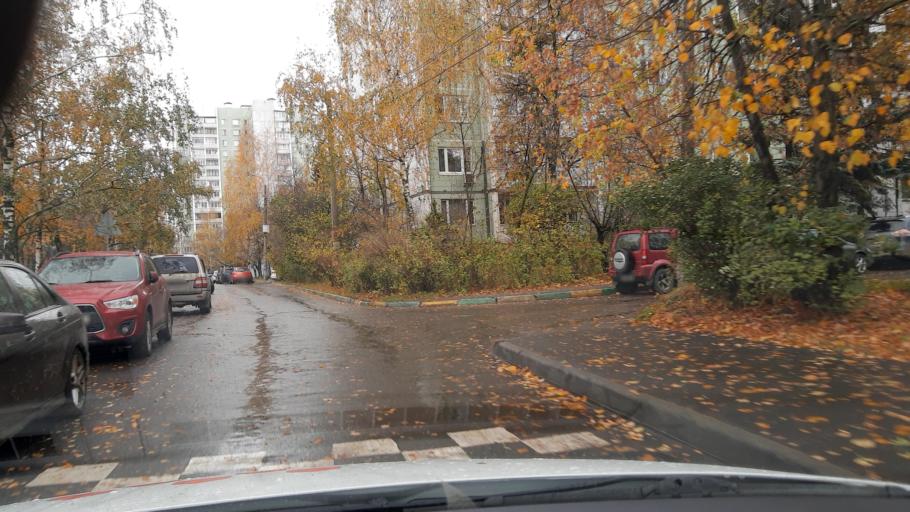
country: RU
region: Moscow
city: Troparevo
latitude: 55.6649
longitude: 37.4957
